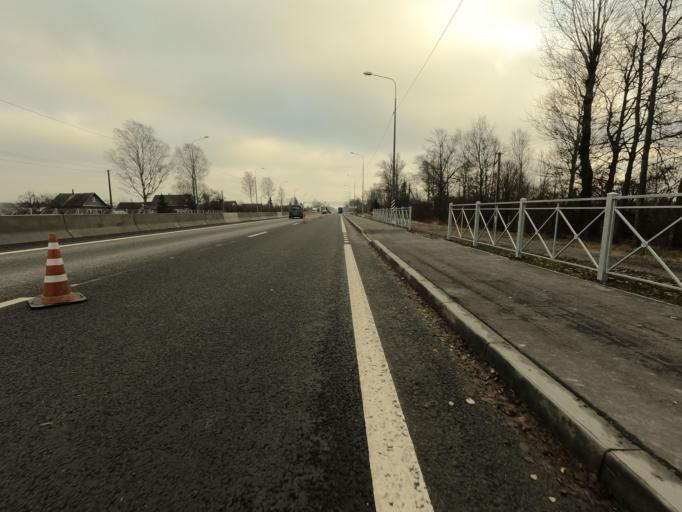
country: RU
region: Leningrad
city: Mga
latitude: 59.7208
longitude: 31.1016
